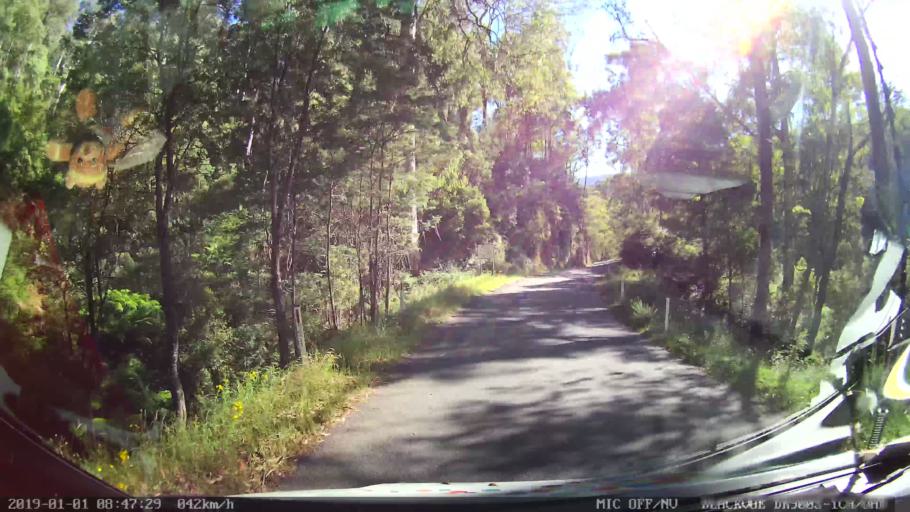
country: AU
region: New South Wales
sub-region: Snowy River
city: Jindabyne
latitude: -36.2940
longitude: 148.1972
